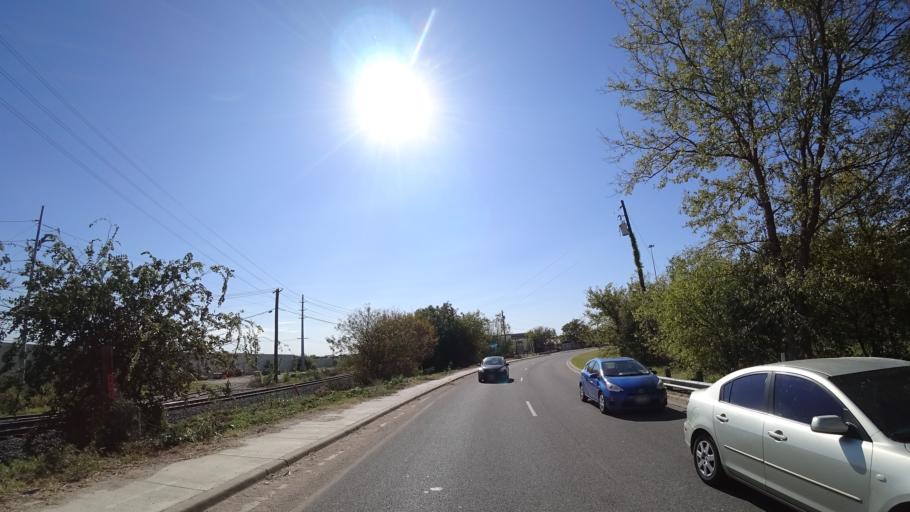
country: US
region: Texas
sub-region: Williamson County
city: Jollyville
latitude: 30.3777
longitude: -97.7368
